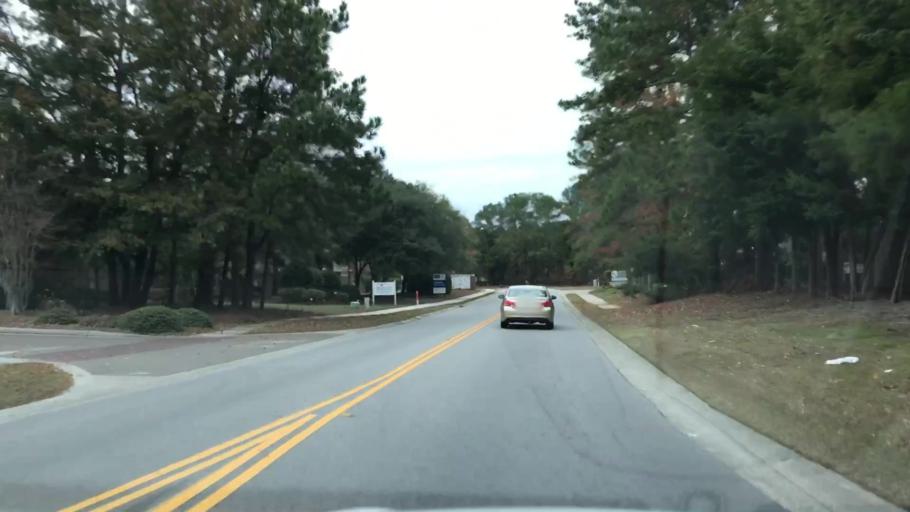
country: US
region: South Carolina
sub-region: Charleston County
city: Mount Pleasant
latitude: 32.8405
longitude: -79.8677
